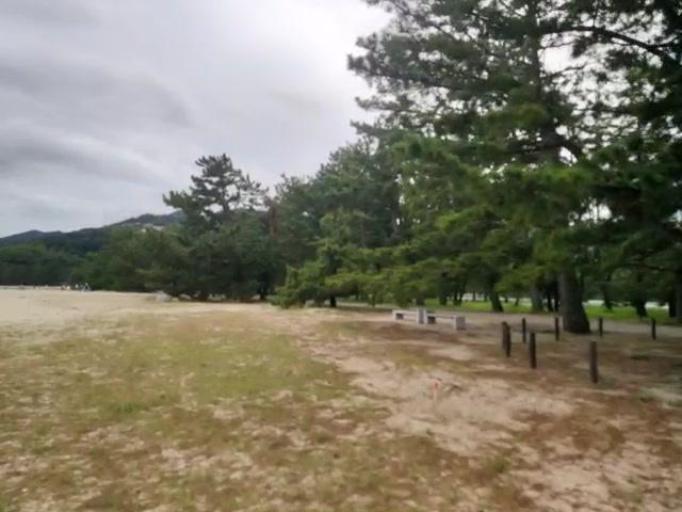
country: JP
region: Kyoto
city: Miyazu
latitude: 35.5605
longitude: 135.1877
